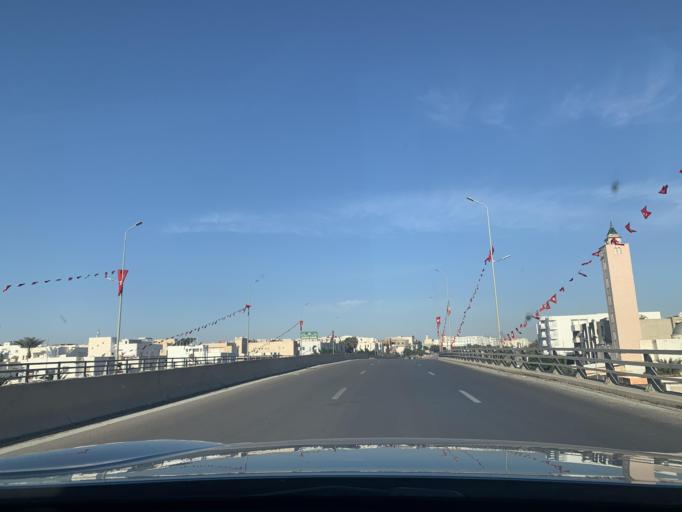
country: DZ
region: Souk Ahras
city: Souk Ahras
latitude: 36.3670
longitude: 8.0003
